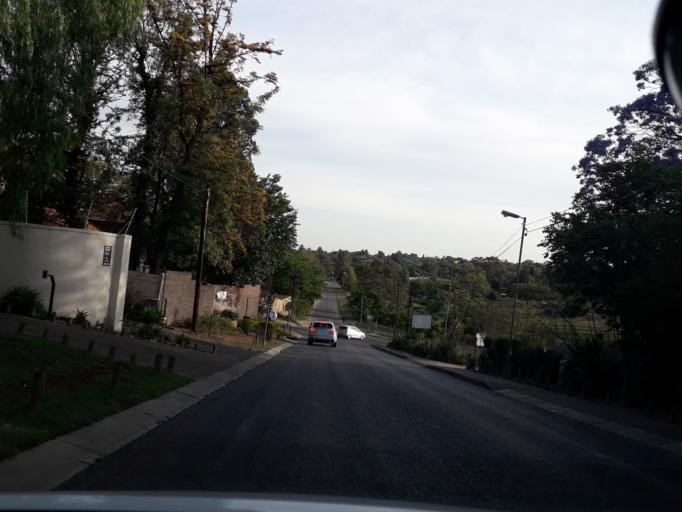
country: ZA
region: Gauteng
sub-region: City of Johannesburg Metropolitan Municipality
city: Johannesburg
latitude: -26.0799
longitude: 27.9897
